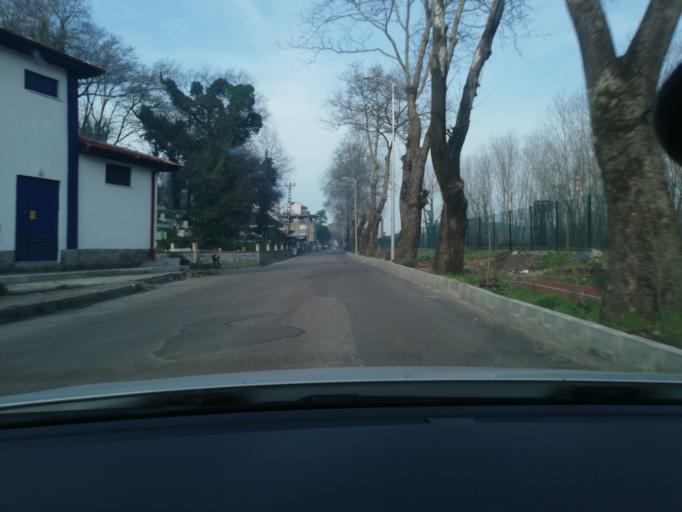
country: TR
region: Zonguldak
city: Kilimli
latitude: 41.5083
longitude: 31.8879
